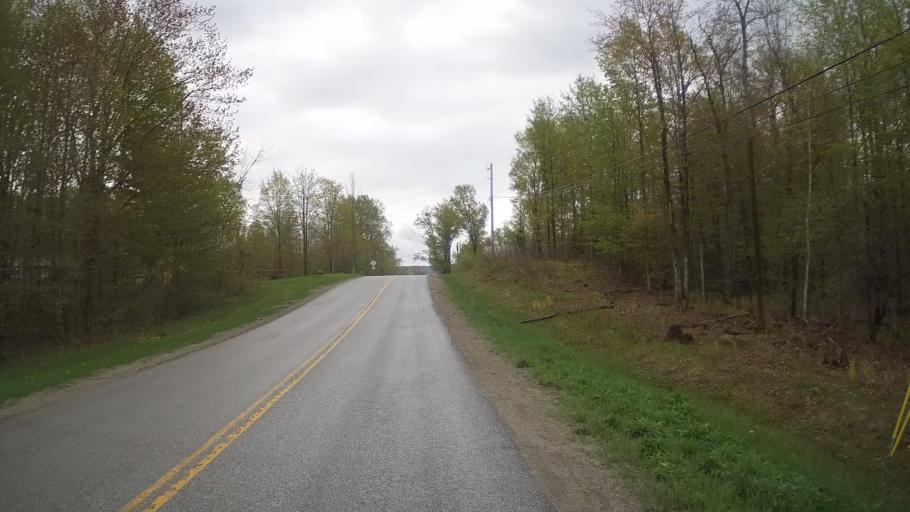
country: US
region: Vermont
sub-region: Franklin County
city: Richford
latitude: 44.9804
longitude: -72.6585
